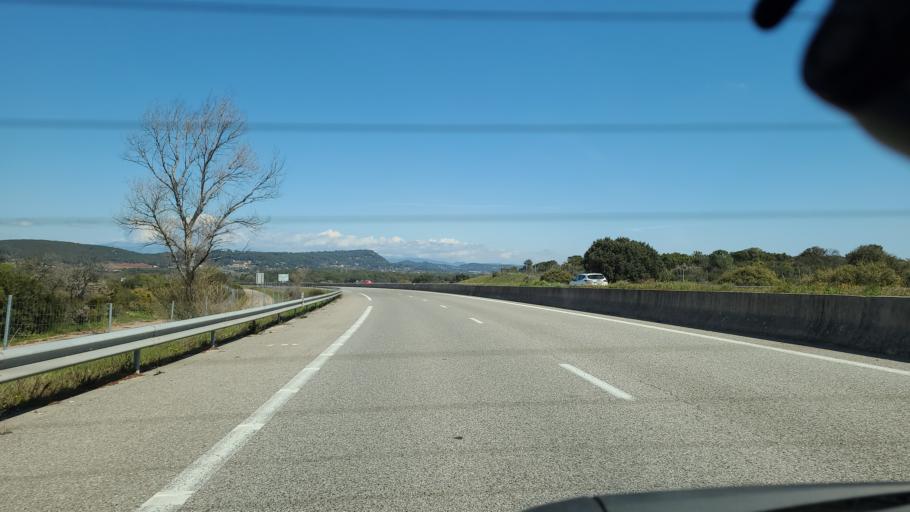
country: FR
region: Provence-Alpes-Cote d'Azur
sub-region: Departement du Var
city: Le Cannet-des-Maures
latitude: 43.3792
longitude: 6.3557
